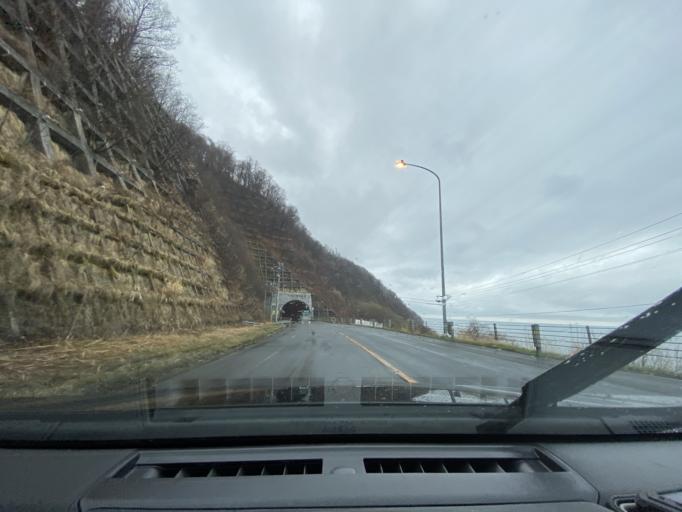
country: JP
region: Hokkaido
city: Rumoi
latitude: 43.8140
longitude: 141.4126
